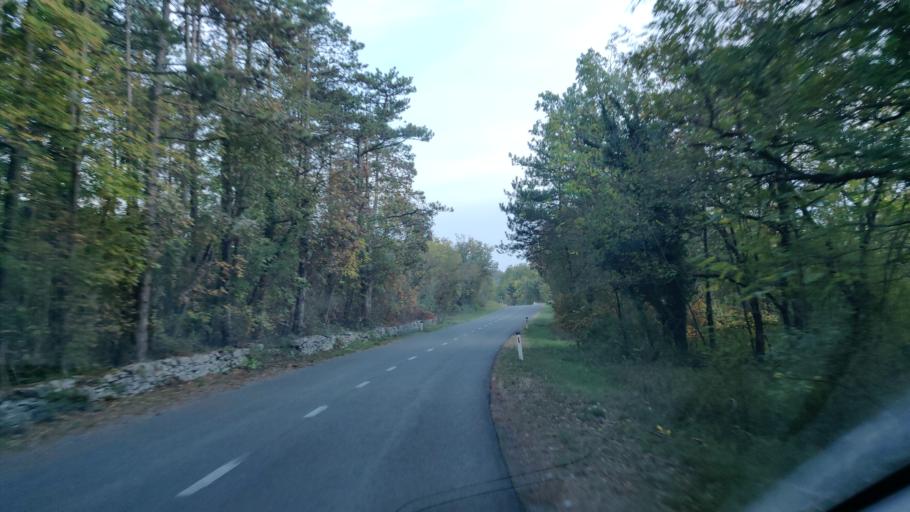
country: SI
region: Sezana
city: Sezana
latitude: 45.7983
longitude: 13.8539
